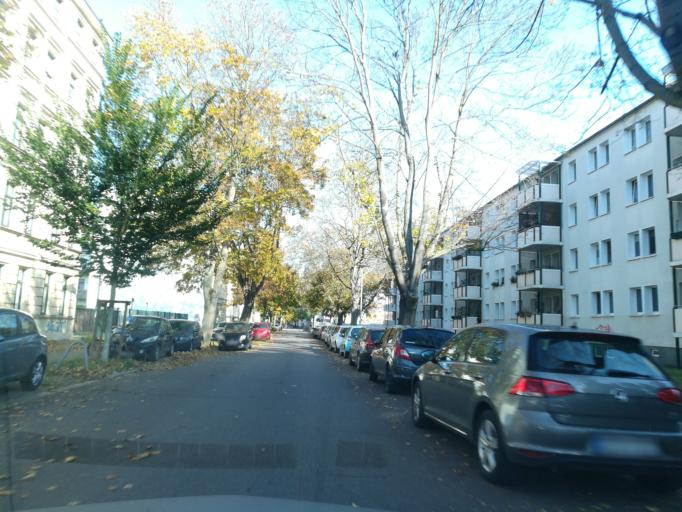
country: DE
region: Saxony-Anhalt
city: Magdeburg
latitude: 52.1287
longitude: 11.6095
